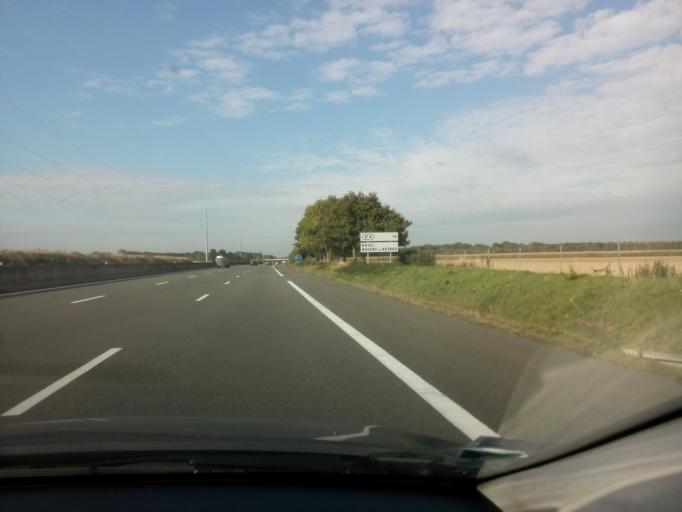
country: FR
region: Centre
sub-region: Departement d'Eure-et-Loir
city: Yevres
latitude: 48.2878
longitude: 1.2591
